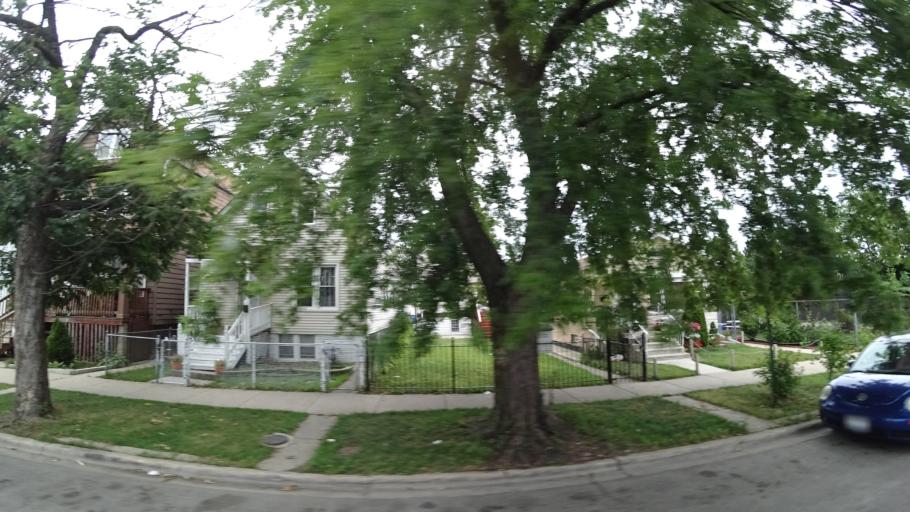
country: US
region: Illinois
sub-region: Cook County
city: Cicero
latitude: 41.8592
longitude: -87.7518
